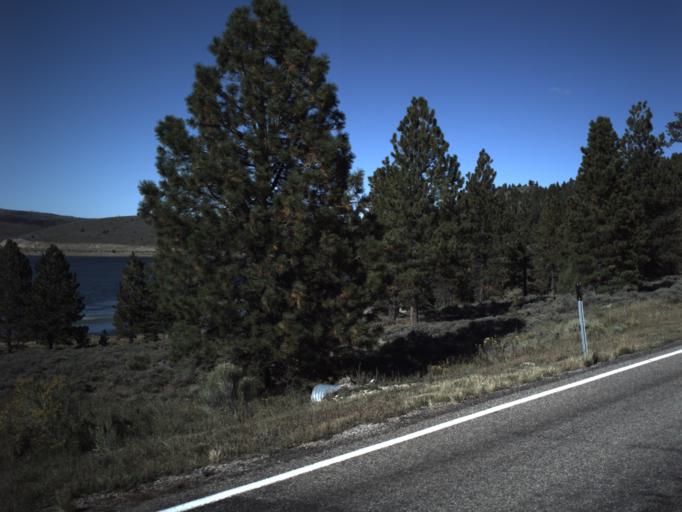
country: US
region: Utah
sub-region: Garfield County
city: Panguitch
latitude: 37.7079
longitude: -112.6277
